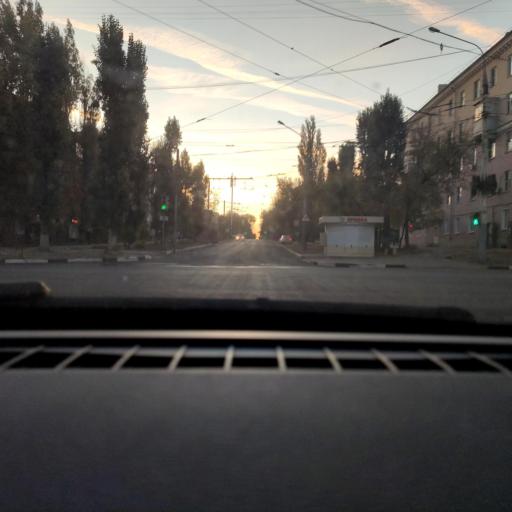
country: RU
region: Voronezj
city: Voronezh
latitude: 51.6395
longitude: 39.2352
